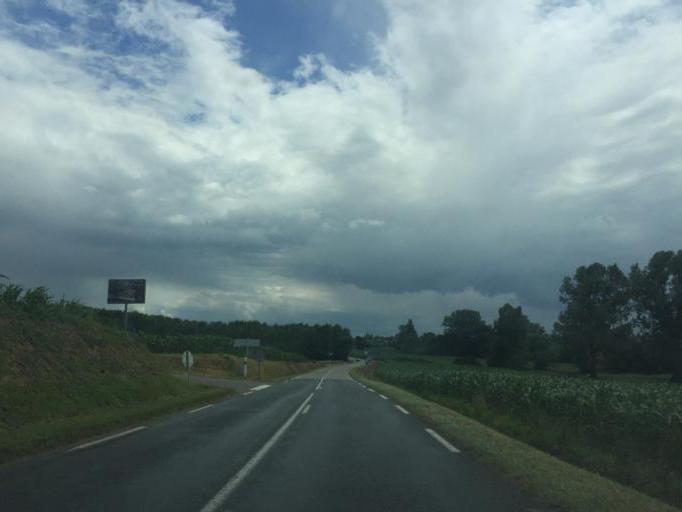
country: FR
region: Rhone-Alpes
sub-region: Departement du Rhone
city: Jons
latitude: 45.7994
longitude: 5.0962
